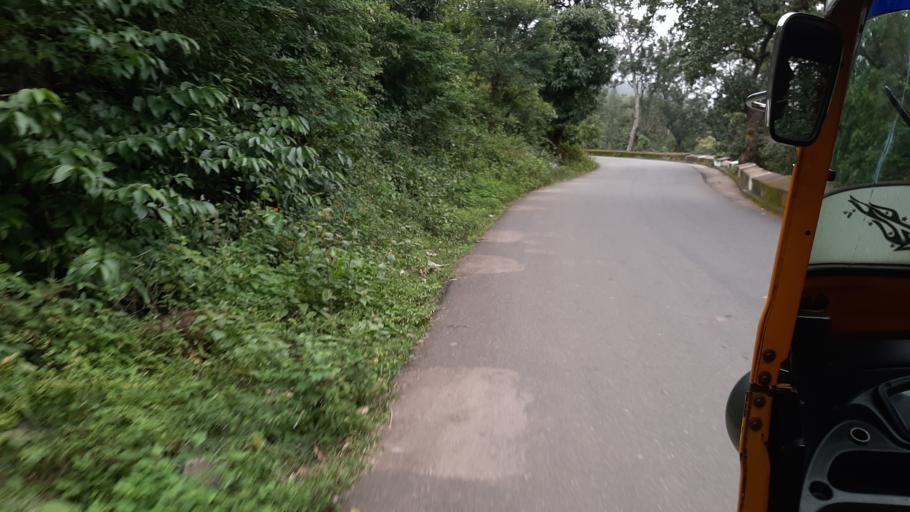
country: IN
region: Andhra Pradesh
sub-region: Vizianagaram District
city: Salur
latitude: 18.2433
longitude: 82.9997
